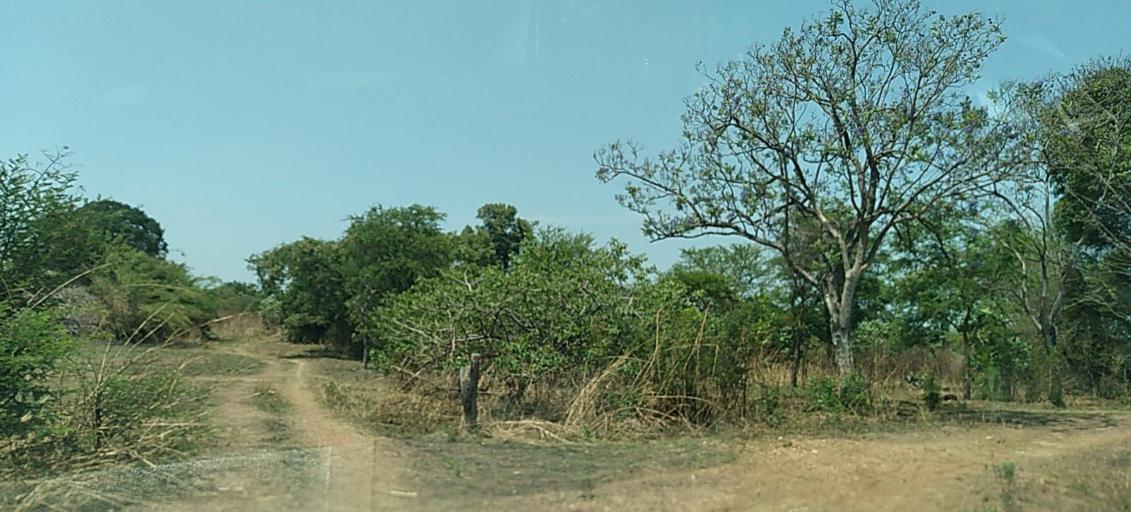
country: ZM
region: Copperbelt
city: Luanshya
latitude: -12.9912
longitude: 28.3254
